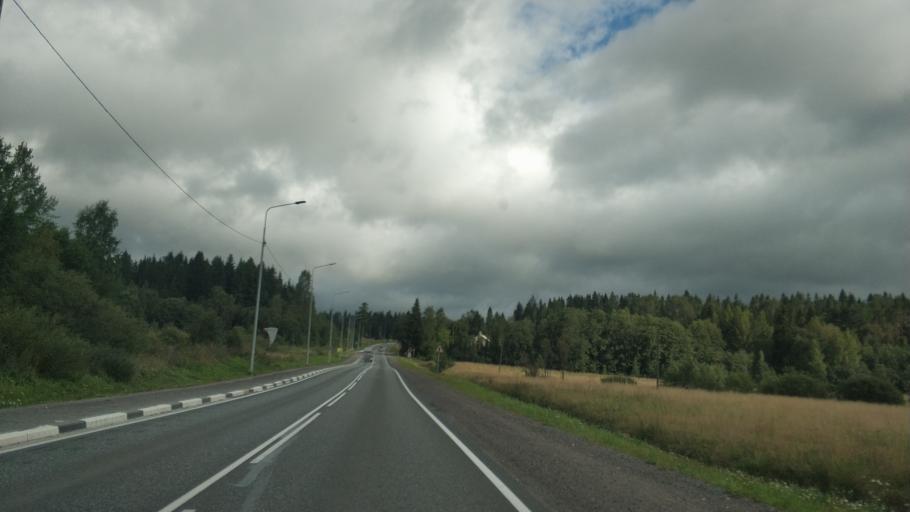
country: RU
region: Republic of Karelia
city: Khelyulya
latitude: 61.7644
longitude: 30.6557
